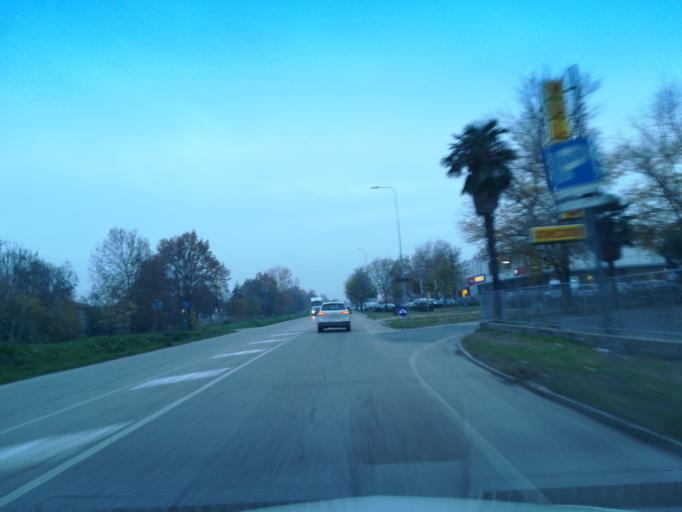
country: IT
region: Emilia-Romagna
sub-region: Provincia di Ravenna
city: Faenza
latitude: 44.3083
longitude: 11.8963
